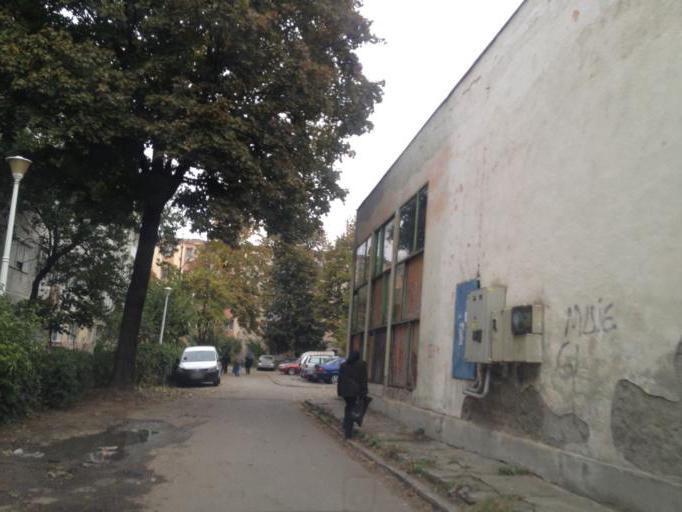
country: RO
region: Dolj
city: Craiova
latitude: 44.3358
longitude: 23.7797
